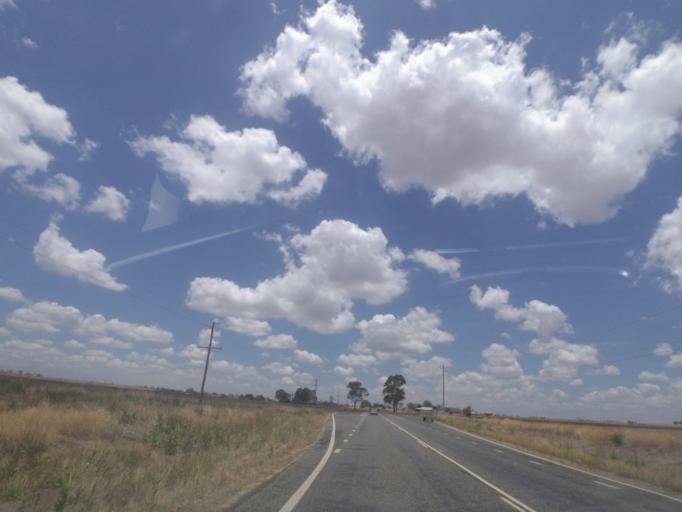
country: AU
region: Queensland
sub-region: Toowoomba
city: Top Camp
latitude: -27.9263
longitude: 151.9846
